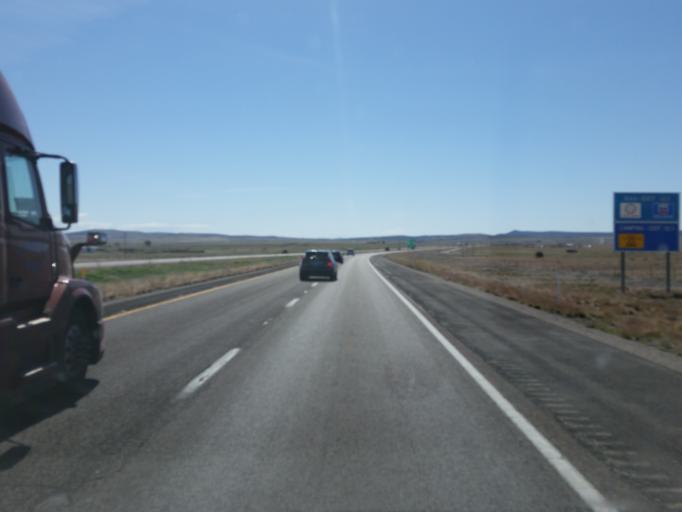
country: US
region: Arizona
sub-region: Yavapai County
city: Paulden
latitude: 35.3159
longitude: -112.8712
